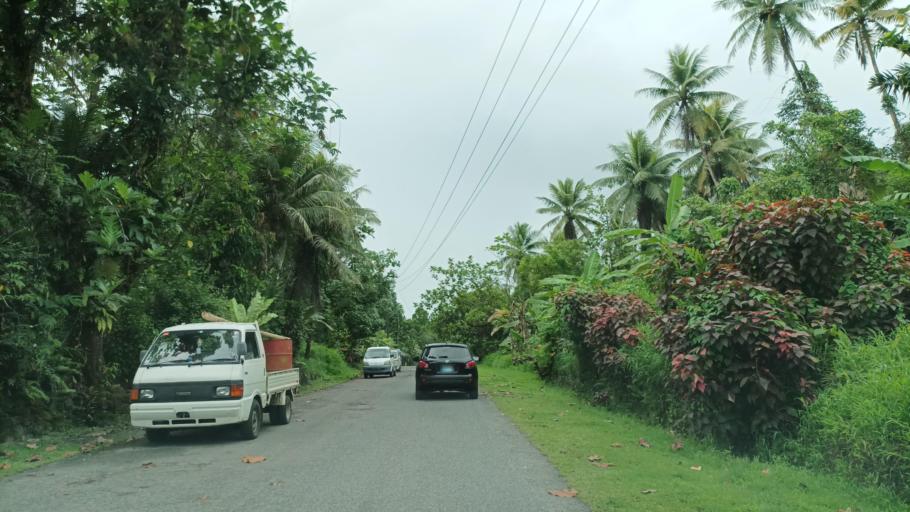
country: FM
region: Pohnpei
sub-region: Kolonia Municipality
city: Kolonia
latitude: 6.9435
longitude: 158.2751
